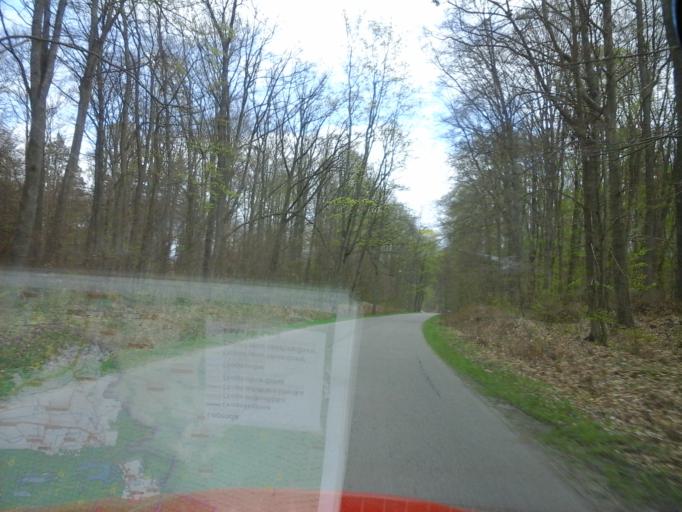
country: PL
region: West Pomeranian Voivodeship
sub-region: Powiat choszczenski
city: Bierzwnik
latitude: 53.0179
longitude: 15.6437
